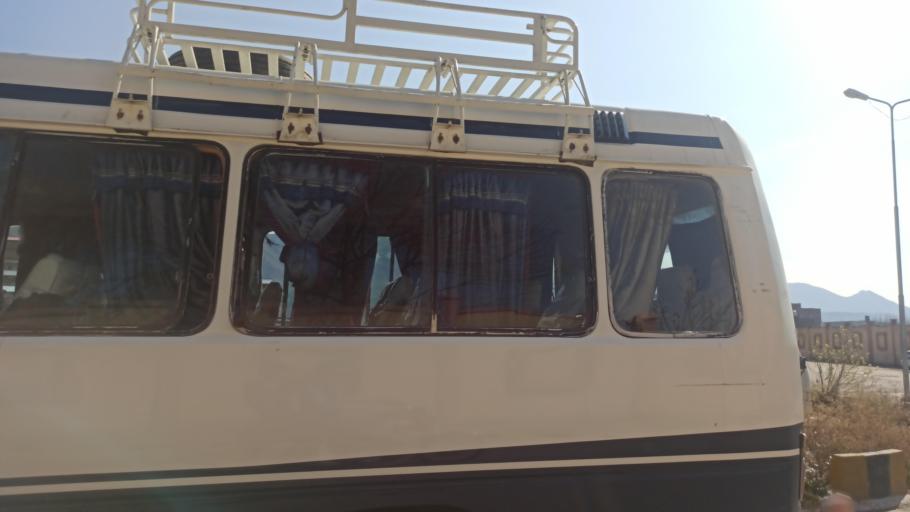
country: PK
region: Khyber Pakhtunkhwa
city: Mingora
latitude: 34.7784
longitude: 72.3315
